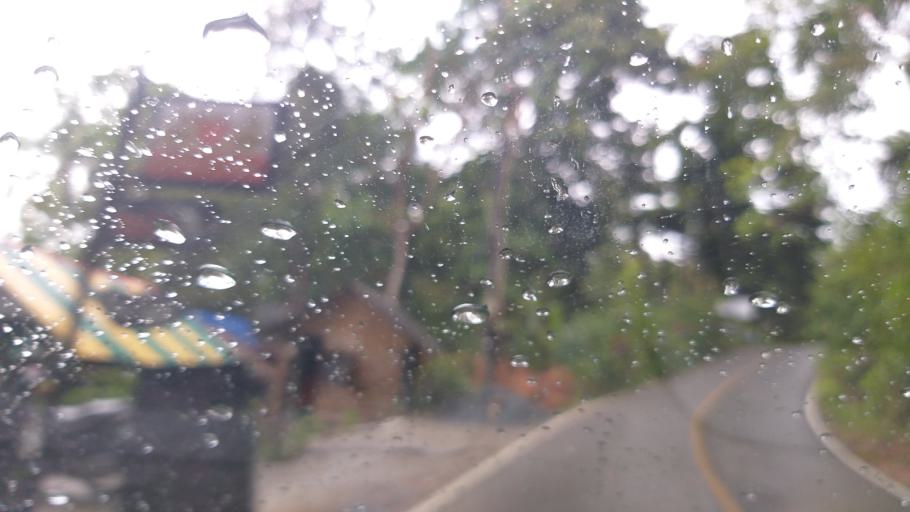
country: TH
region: Trat
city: Ko Chang Tai
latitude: 11.9744
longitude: 102.3207
